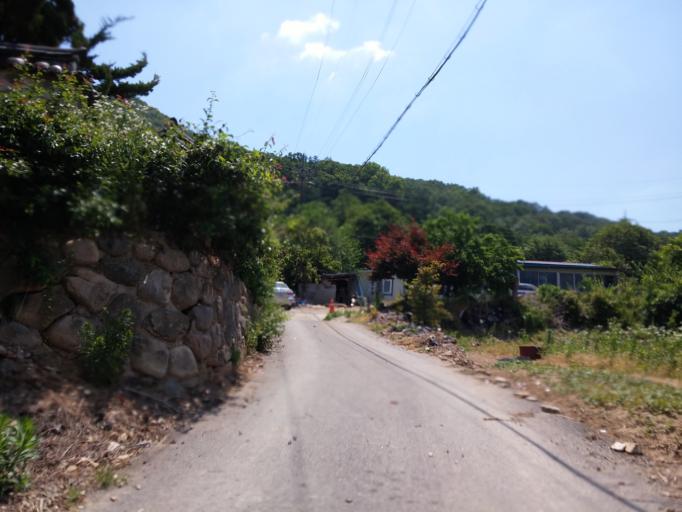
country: KR
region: Chungcheongbuk-do
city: Cheongju-si
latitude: 36.5539
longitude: 127.4375
